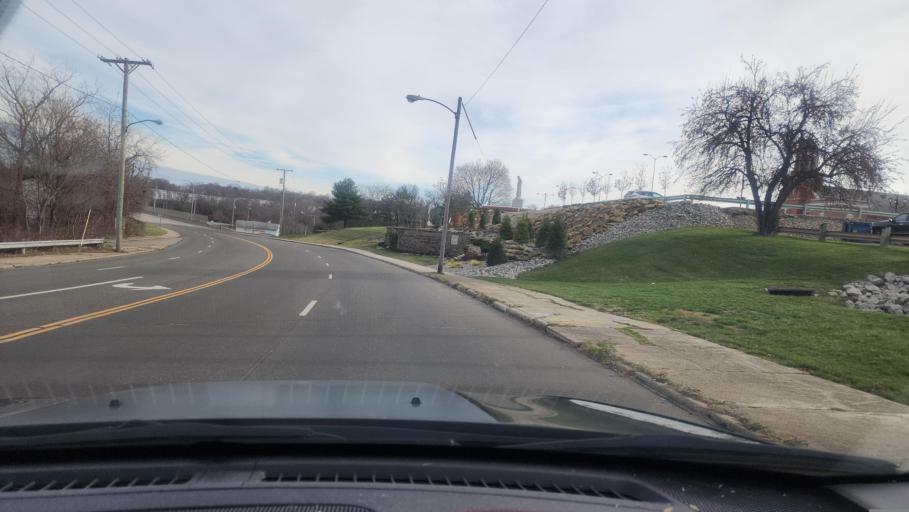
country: US
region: Ohio
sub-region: Mahoning County
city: Youngstown
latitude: 41.1009
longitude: -80.6426
